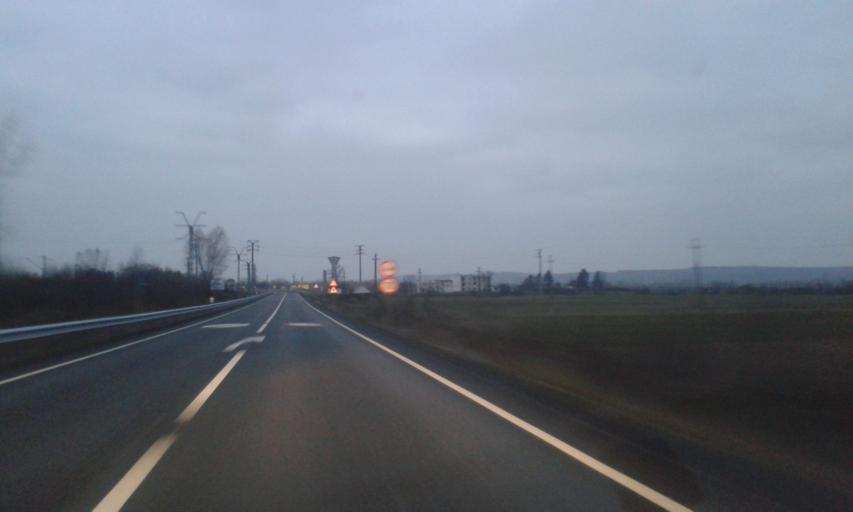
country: RO
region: Gorj
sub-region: Comuna Turcinesti
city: Turcinesti
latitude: 45.1170
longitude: 23.3477
